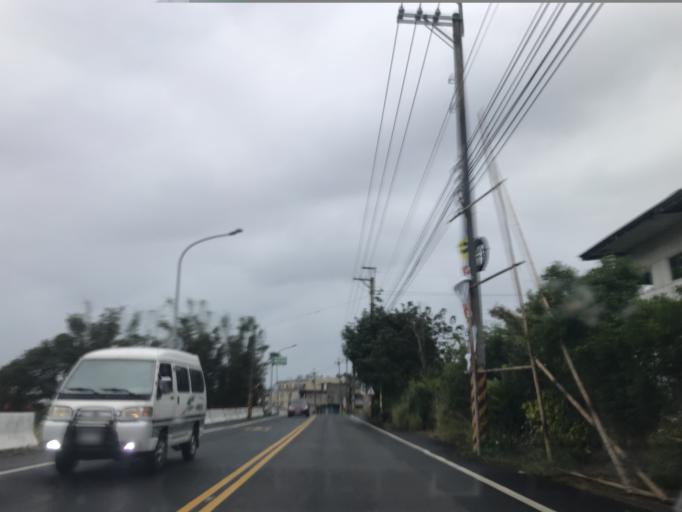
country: TW
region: Taiwan
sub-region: Hsinchu
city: Zhubei
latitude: 24.8310
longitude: 121.0864
